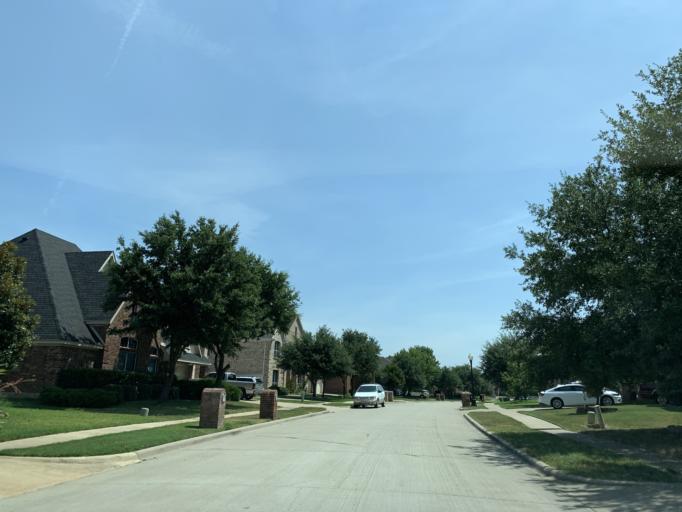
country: US
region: Texas
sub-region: Dallas County
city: Cedar Hill
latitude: 32.6403
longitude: -97.0403
